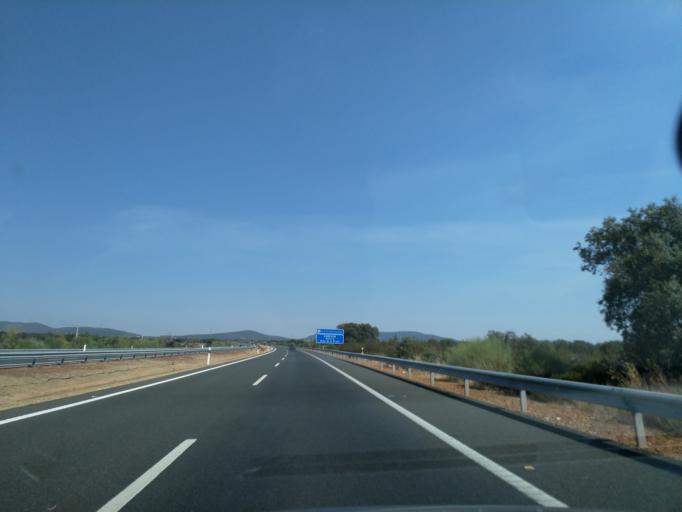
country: ES
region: Extremadura
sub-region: Provincia de Badajoz
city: Aljucen
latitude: 39.1014
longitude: -6.2846
